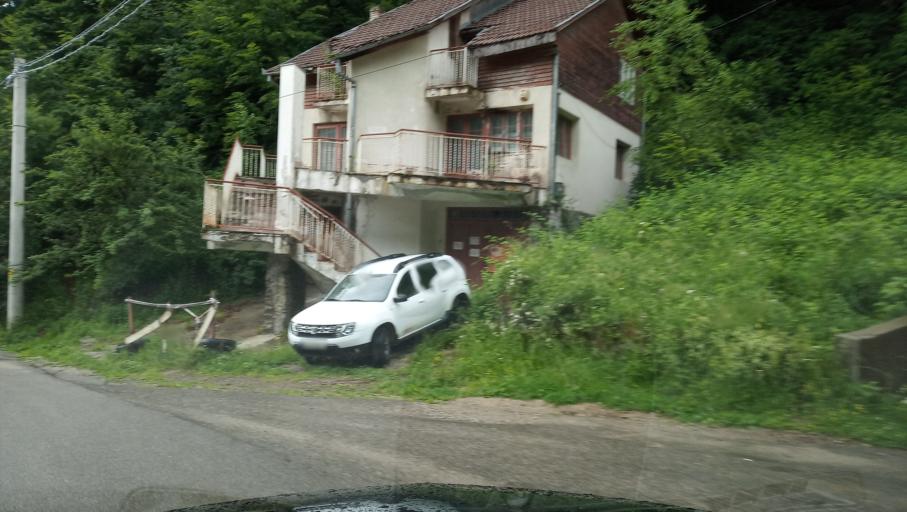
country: RO
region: Hunedoara
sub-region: Oras Petrila
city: Petrila
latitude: 45.3934
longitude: 23.4459
